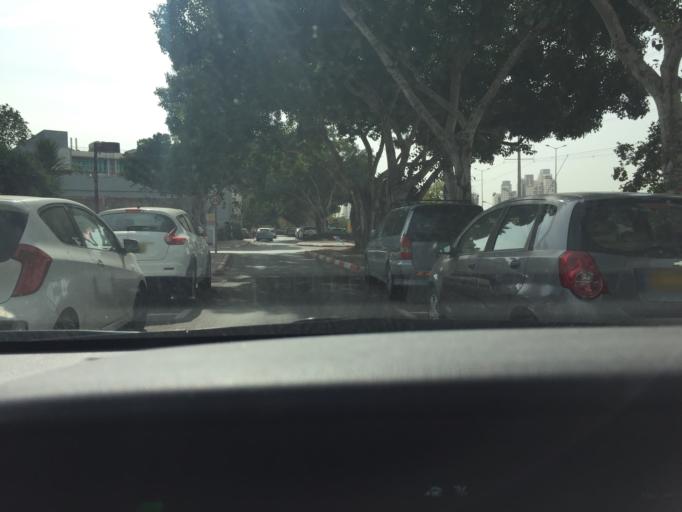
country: IL
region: Tel Aviv
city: Giv`at Shemu'el
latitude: 32.0686
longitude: 34.8413
